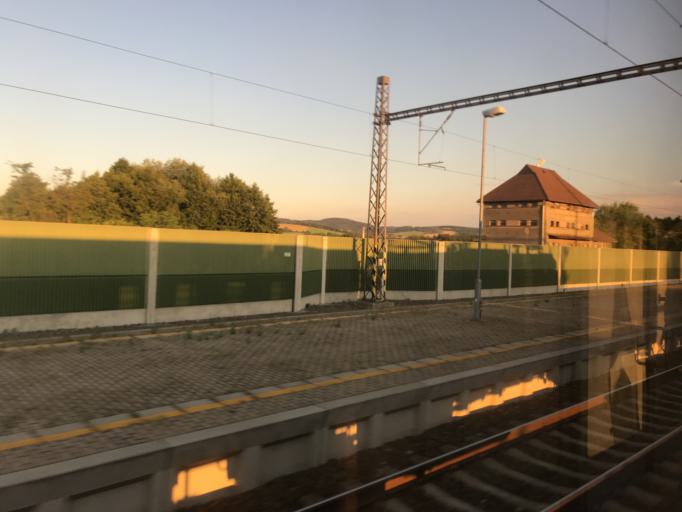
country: CZ
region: Central Bohemia
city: Votice
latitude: 49.6688
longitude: 14.6251
